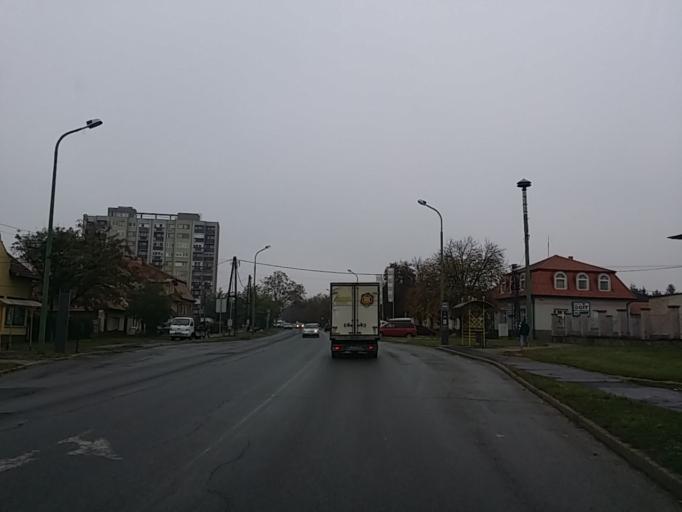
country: HU
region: Heves
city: Gyongyos
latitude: 47.7742
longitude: 19.9218
